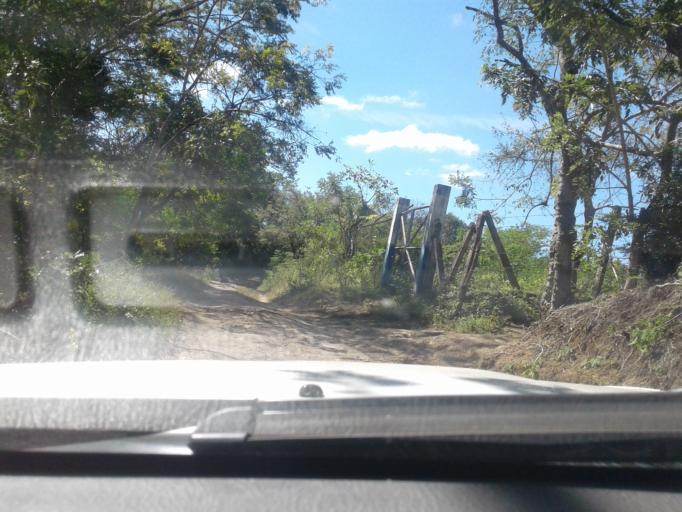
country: NI
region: Carazo
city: Santa Teresa
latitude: 11.7800
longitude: -86.1869
